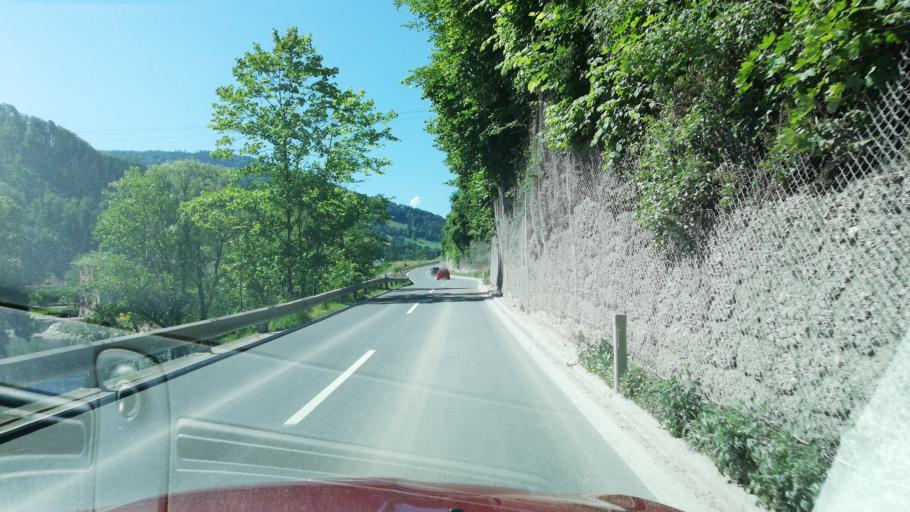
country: AT
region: Upper Austria
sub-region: Politischer Bezirk Kirchdorf an der Krems
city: Gruenburg
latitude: 47.9519
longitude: 14.2559
